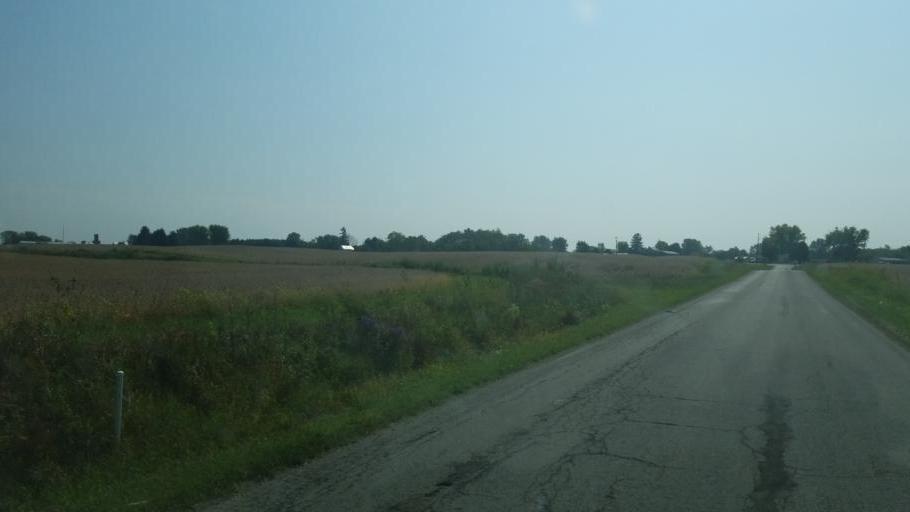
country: US
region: Ohio
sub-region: Crawford County
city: Galion
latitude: 40.6646
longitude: -82.8396
